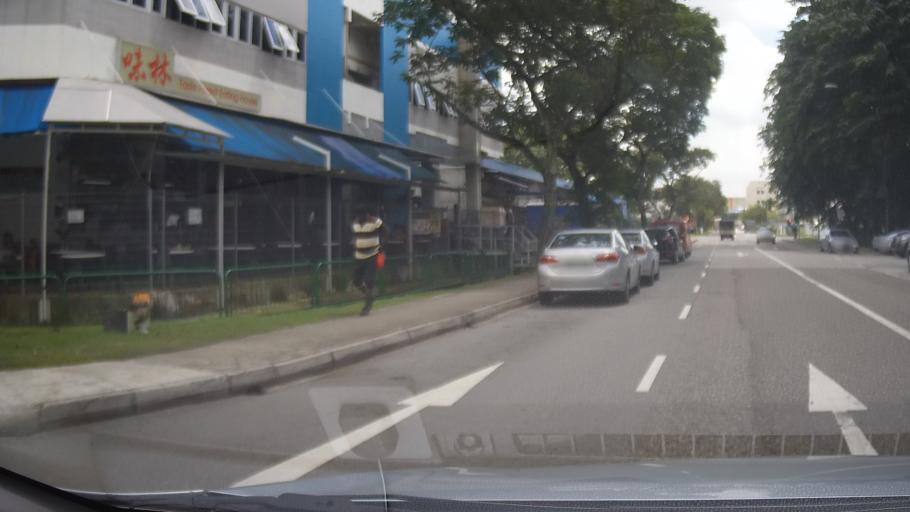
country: MY
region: Johor
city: Johor Bahru
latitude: 1.3291
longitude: 103.6880
